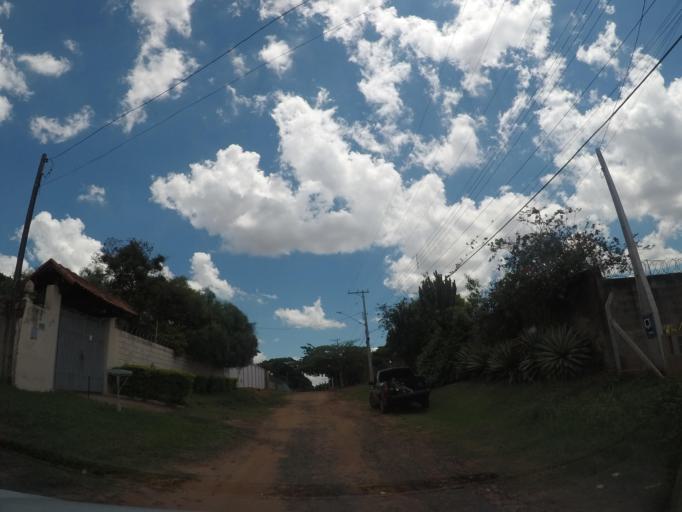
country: BR
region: Sao Paulo
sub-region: Hortolandia
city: Hortolandia
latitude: -22.8427
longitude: -47.2386
